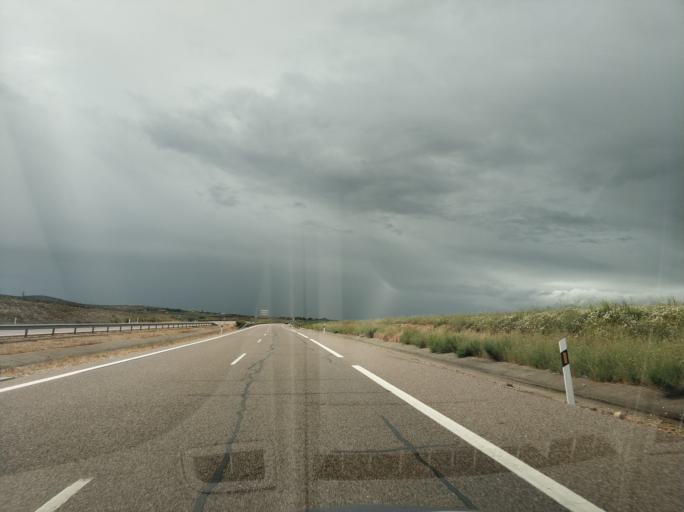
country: ES
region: Castille and Leon
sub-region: Provincia de Salamanca
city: Aldeatejada
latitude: 40.9247
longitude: -5.6713
